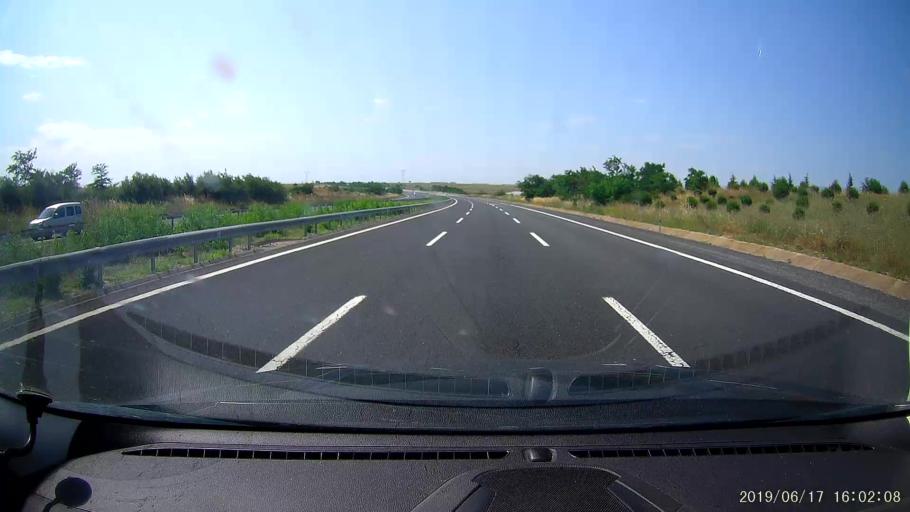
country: TR
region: Tekirdag
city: Velimese
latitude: 41.2561
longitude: 27.8309
